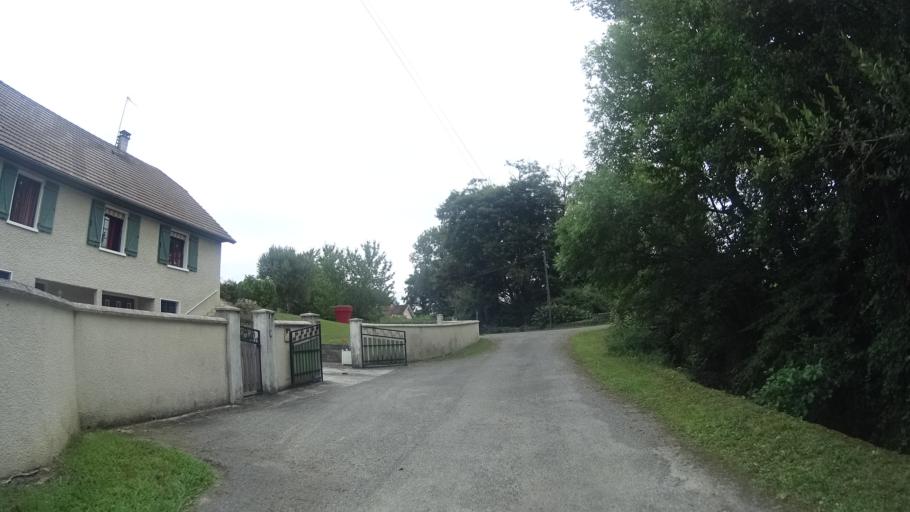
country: FR
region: Aquitaine
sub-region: Departement des Pyrenees-Atlantiques
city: Orthez
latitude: 43.4701
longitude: -0.7121
